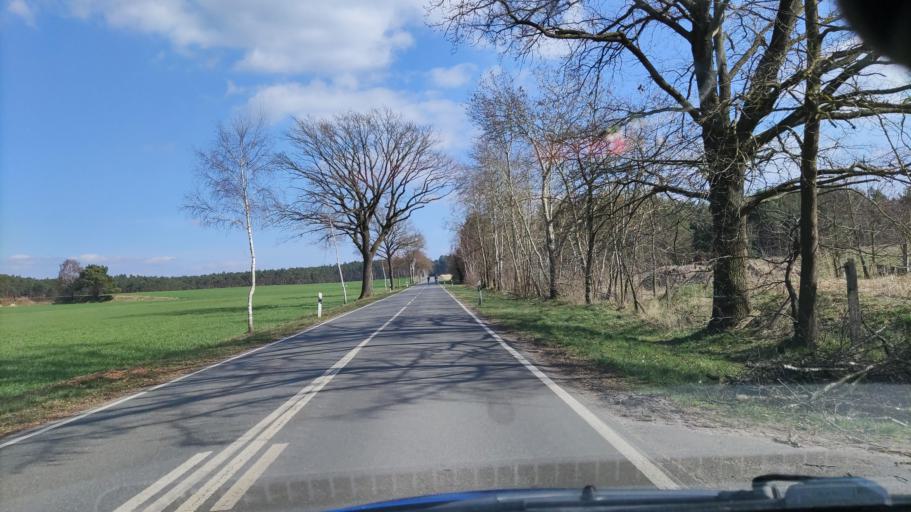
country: DE
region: Lower Saxony
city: Trebel
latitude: 53.0302
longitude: 11.3086
